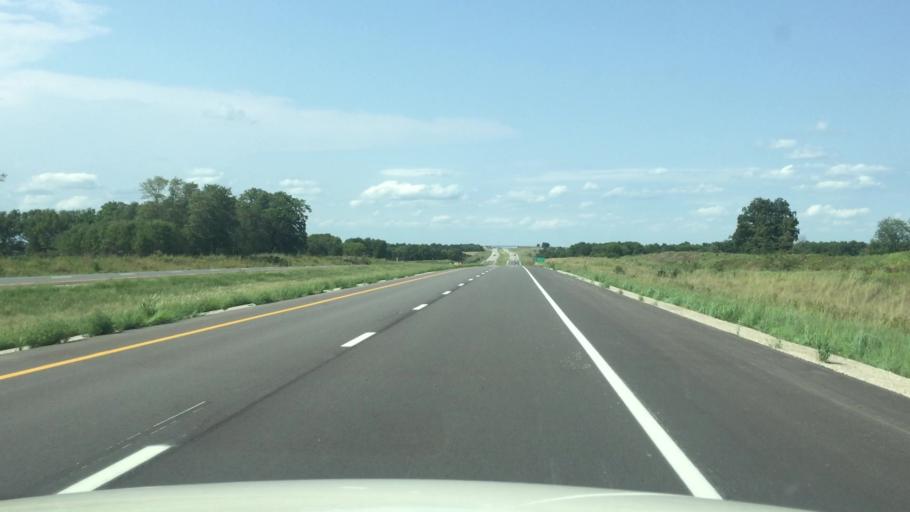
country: US
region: Kansas
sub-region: Linn County
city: La Cygne
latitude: 38.3794
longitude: -94.6874
